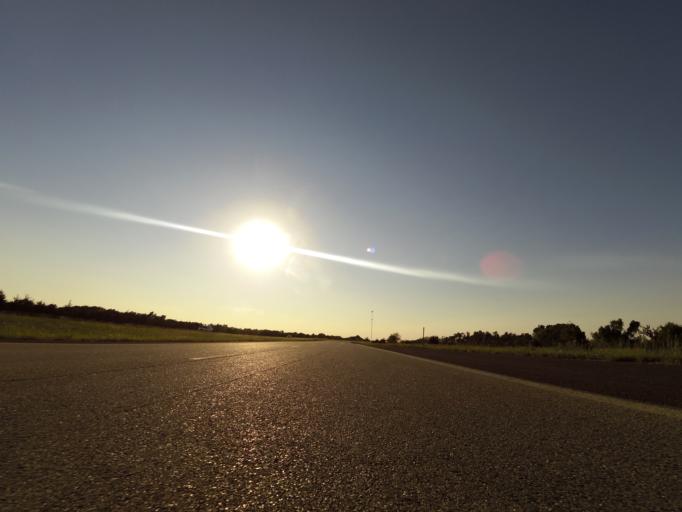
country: US
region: Kansas
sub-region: Reno County
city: South Hutchinson
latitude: 37.9665
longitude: -97.9263
